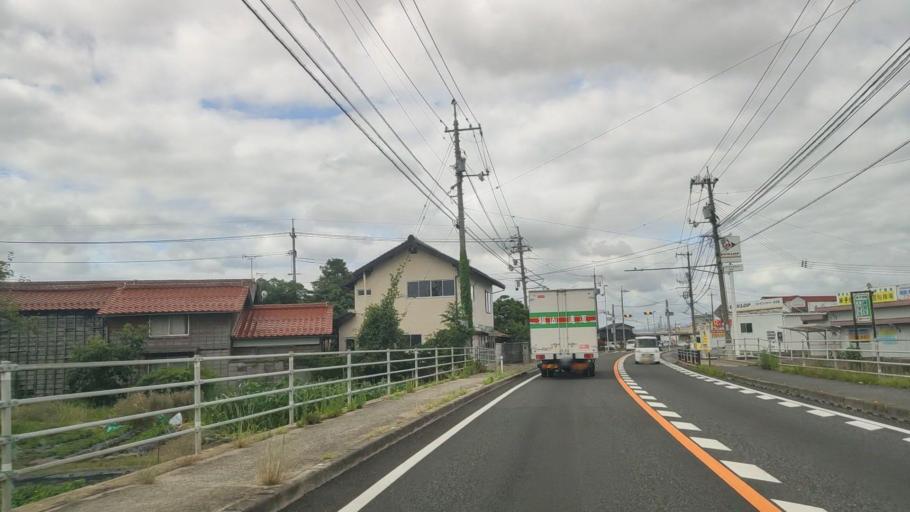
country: JP
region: Tottori
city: Yonago
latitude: 35.4344
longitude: 133.3873
